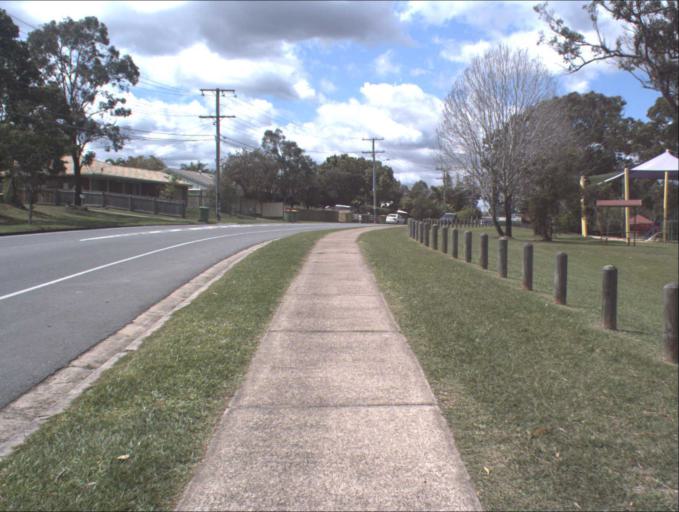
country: AU
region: Queensland
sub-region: Brisbane
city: Sunnybank Hills
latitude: -27.6633
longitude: 153.0330
